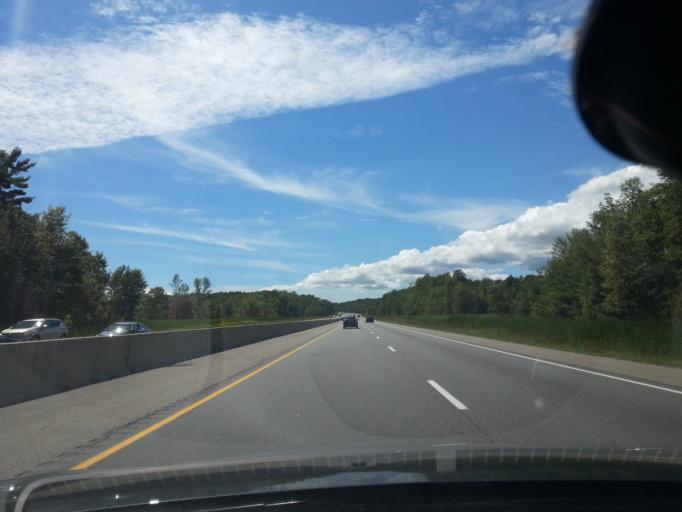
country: CA
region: Ontario
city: Brockville
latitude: 44.5599
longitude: -75.7515
